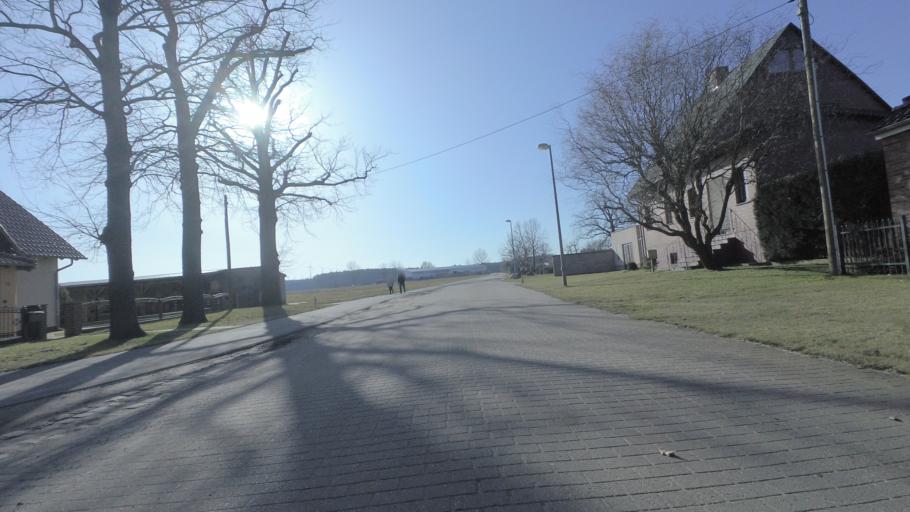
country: DE
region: Brandenburg
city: Luckenwalde
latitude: 52.0587
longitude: 13.1668
